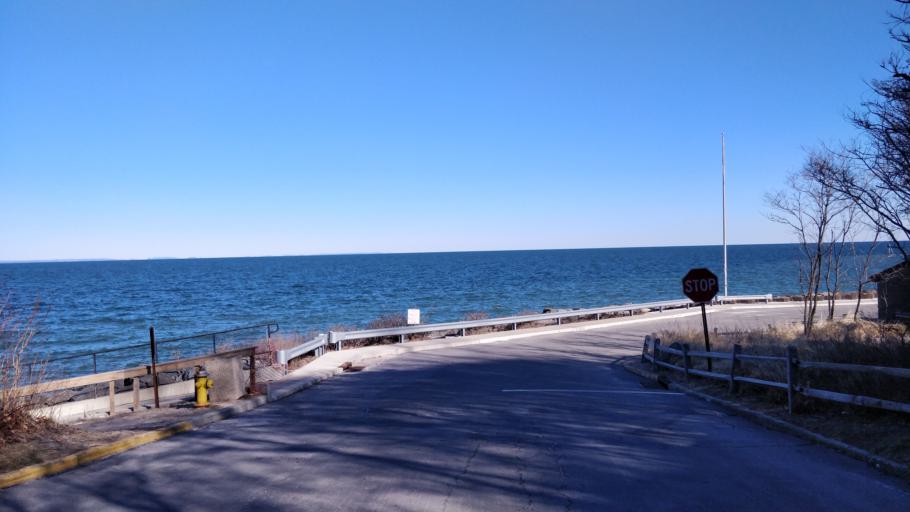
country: US
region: New York
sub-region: Suffolk County
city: Mount Sinai
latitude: 40.9639
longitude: -73.0496
